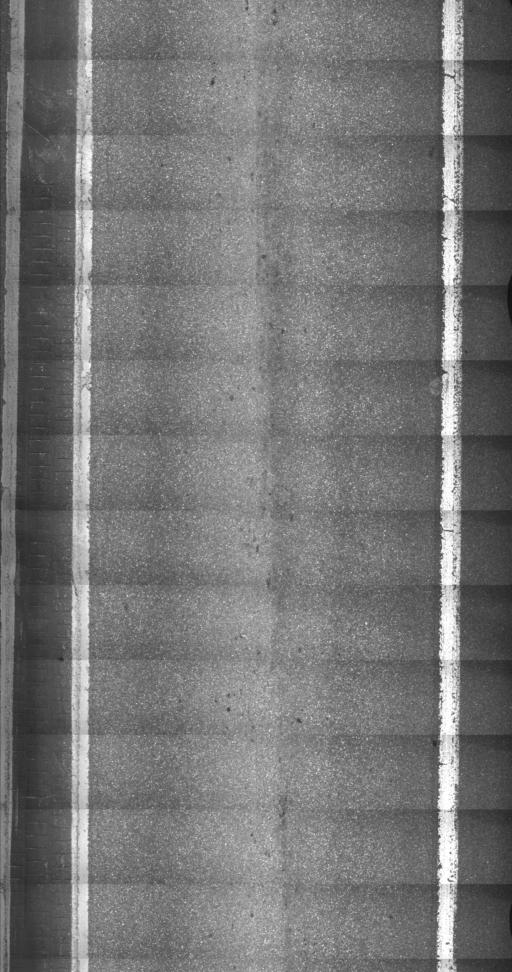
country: US
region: Vermont
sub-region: Chittenden County
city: Burlington
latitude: 44.4725
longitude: -73.2052
